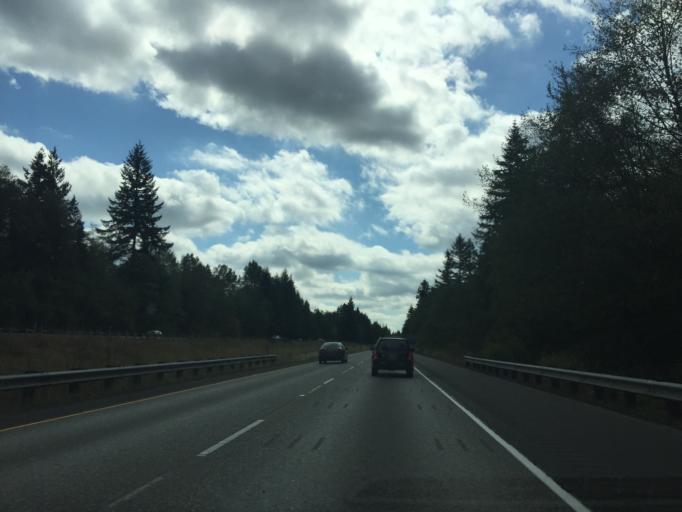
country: US
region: Washington
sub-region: Whatcom County
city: Sudden Valley
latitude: 48.5996
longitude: -122.3447
